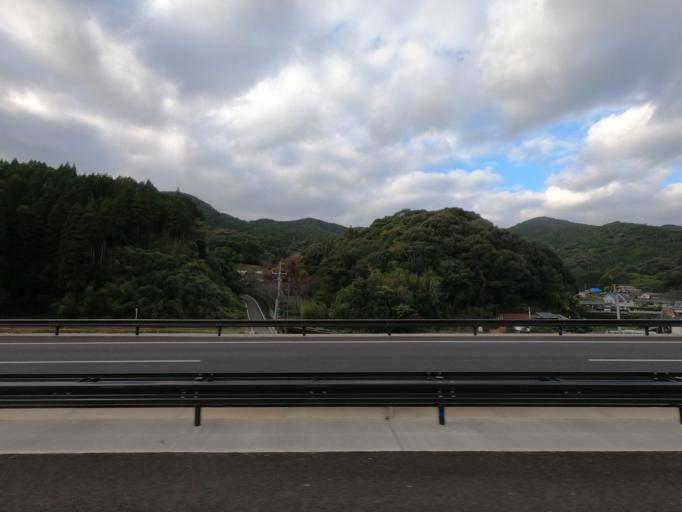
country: JP
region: Kumamoto
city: Minamata
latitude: 32.2402
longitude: 130.4630
